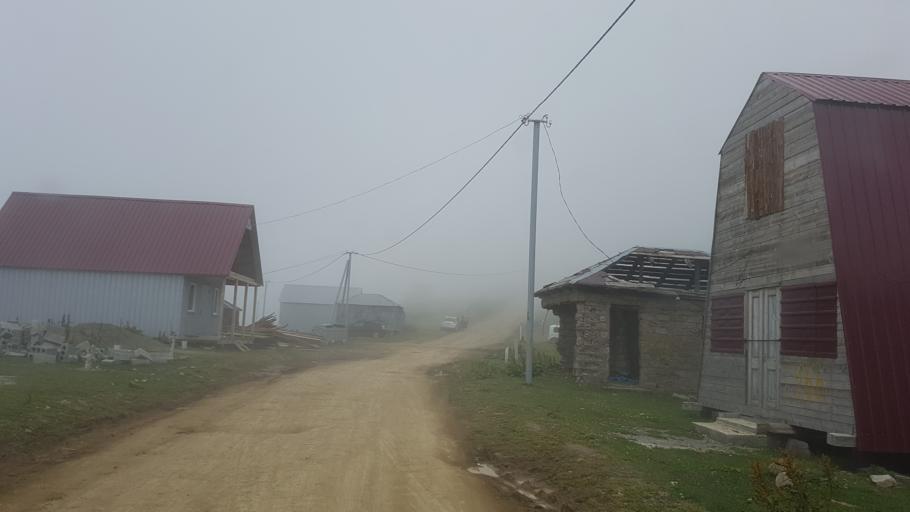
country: GE
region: Ajaria
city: Akhaldaba
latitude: 41.8243
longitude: 42.1583
